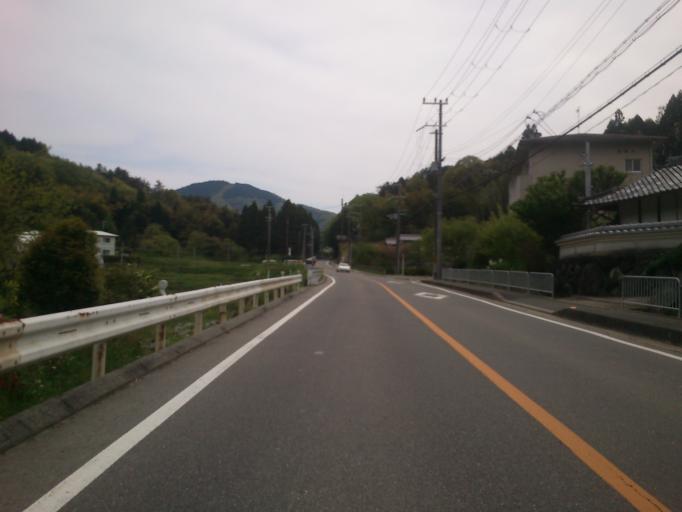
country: JP
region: Kyoto
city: Kameoka
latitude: 34.9657
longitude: 135.5131
